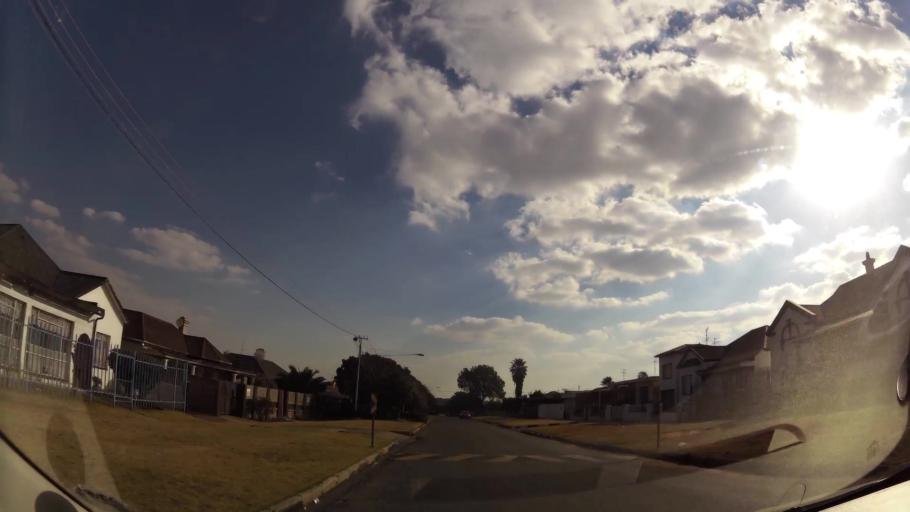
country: ZA
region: Gauteng
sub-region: West Rand District Municipality
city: Krugersdorp
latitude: -26.0930
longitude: 27.7677
